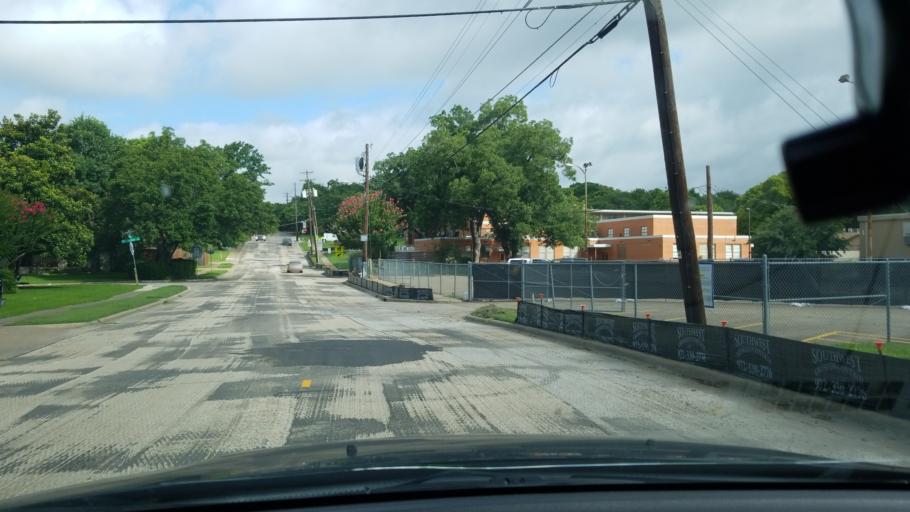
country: US
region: Texas
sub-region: Dallas County
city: Highland Park
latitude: 32.8123
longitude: -96.7095
